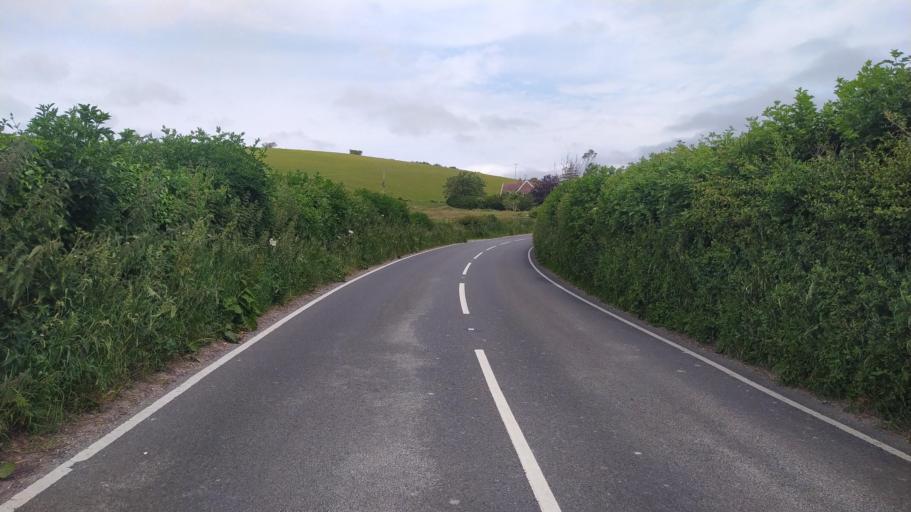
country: GB
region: England
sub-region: Dorset
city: Dorchester
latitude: 50.7918
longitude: -2.4780
